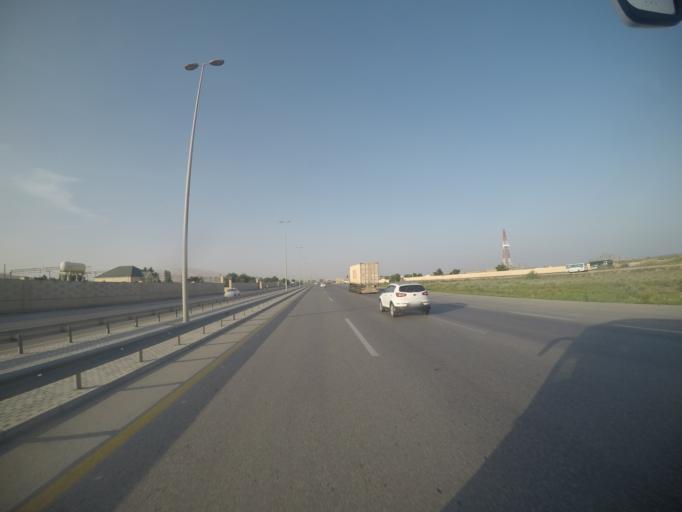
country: AZ
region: Baki
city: Korgoz
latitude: 40.2385
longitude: 49.5930
